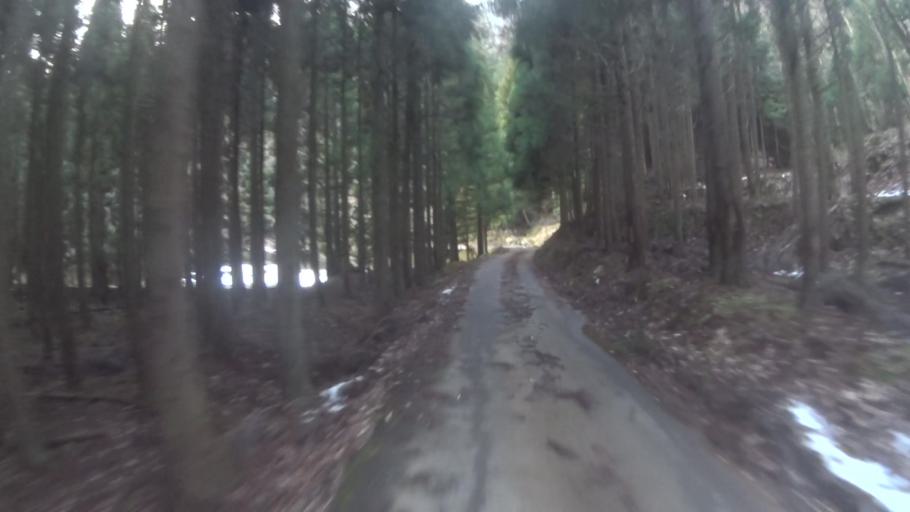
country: JP
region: Kyoto
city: Maizuru
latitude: 35.3992
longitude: 135.4924
